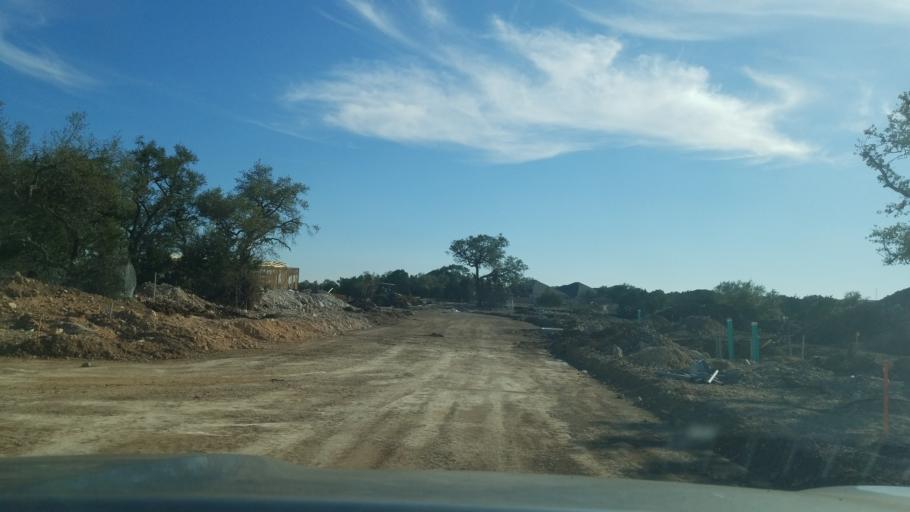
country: US
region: Texas
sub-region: Comal County
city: Canyon Lake
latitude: 29.7833
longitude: -98.2860
